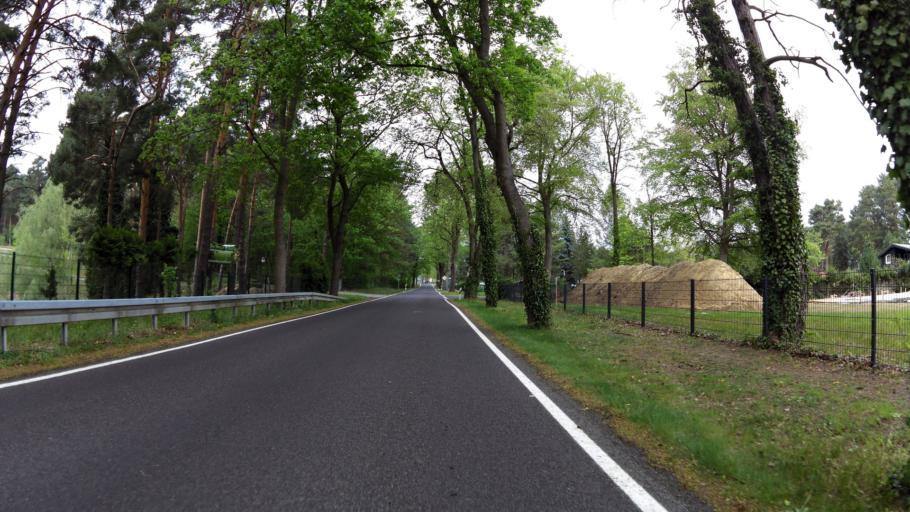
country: DE
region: Brandenburg
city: Mittenwalde
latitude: 52.2006
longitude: 13.5739
